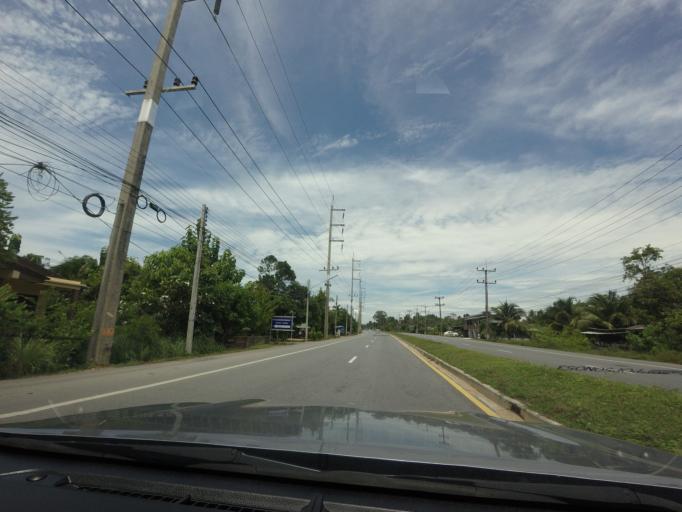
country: TH
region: Songkhla
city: Krasae Sin
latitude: 7.6164
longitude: 100.3969
